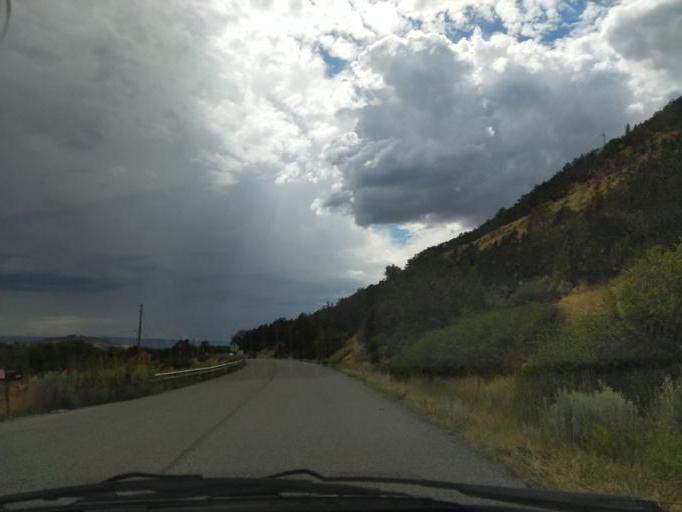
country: US
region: Colorado
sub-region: Delta County
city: Paonia
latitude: 38.9005
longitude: -107.5648
